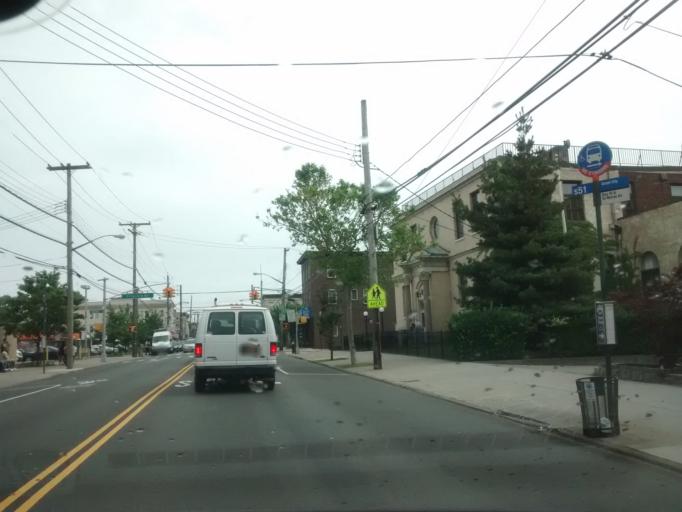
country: US
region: New Jersey
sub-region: Hudson County
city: Bayonne
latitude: 40.6162
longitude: -74.0677
